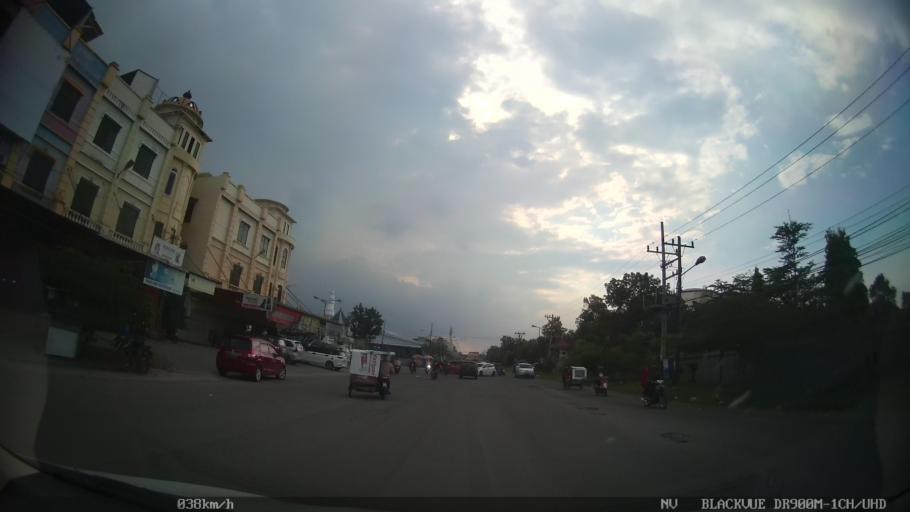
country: ID
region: North Sumatra
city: Medan
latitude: 3.6063
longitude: 98.7108
